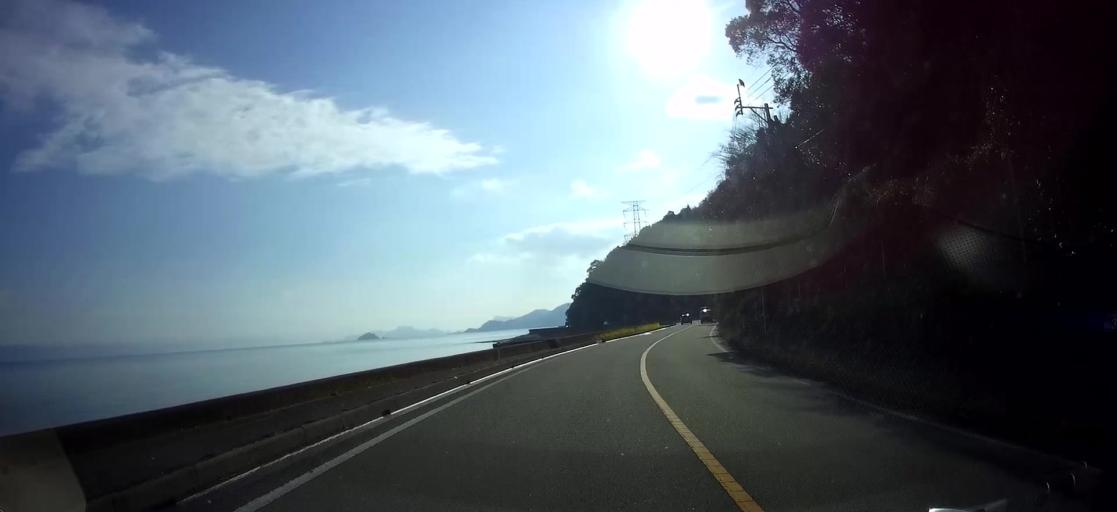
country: JP
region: Kumamoto
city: Yatsushiro
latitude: 32.5067
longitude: 130.4521
